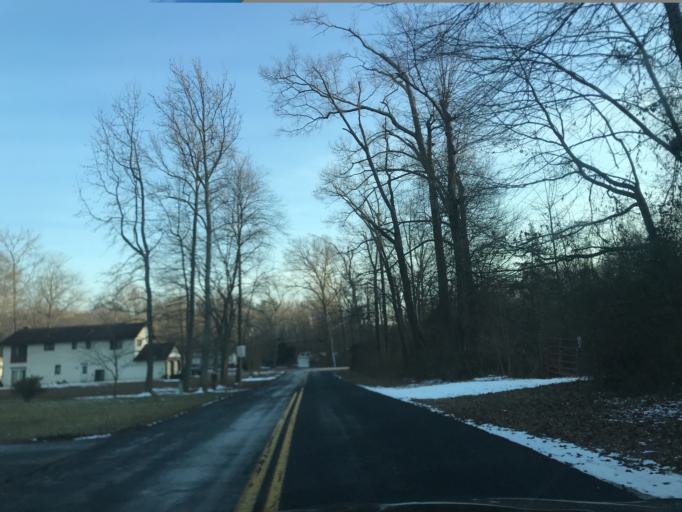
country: US
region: Maryland
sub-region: Harford County
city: Riverside
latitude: 39.4363
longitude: -76.2553
